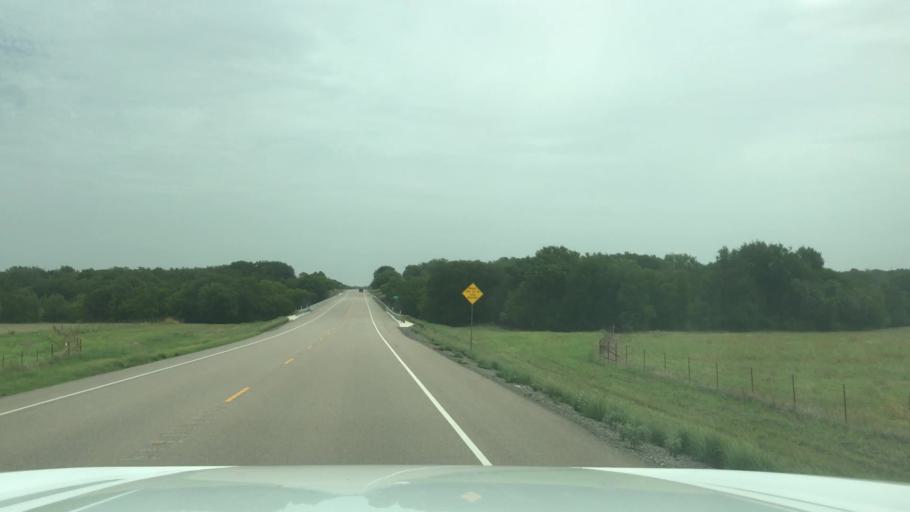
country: US
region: Texas
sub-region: Hamilton County
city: Hico
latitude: 31.9777
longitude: -97.8983
